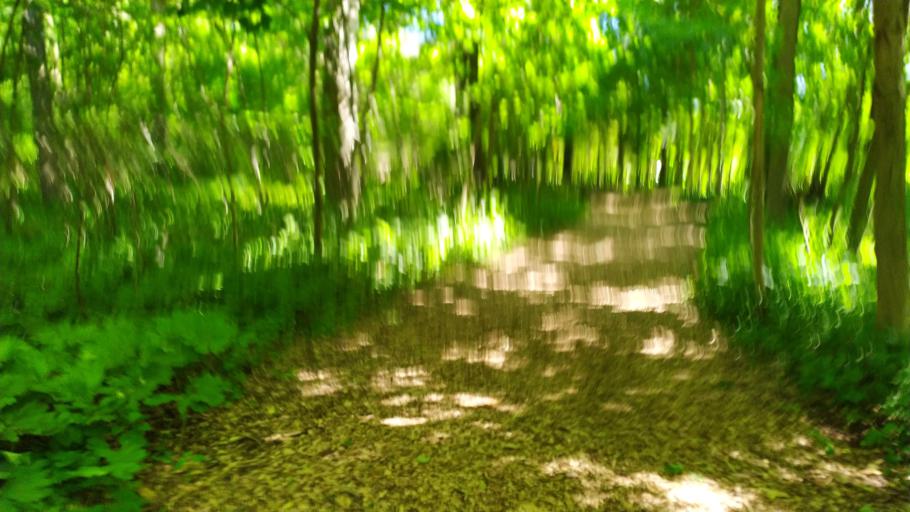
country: CA
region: Ontario
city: Stratford
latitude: 43.3696
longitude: -81.0005
